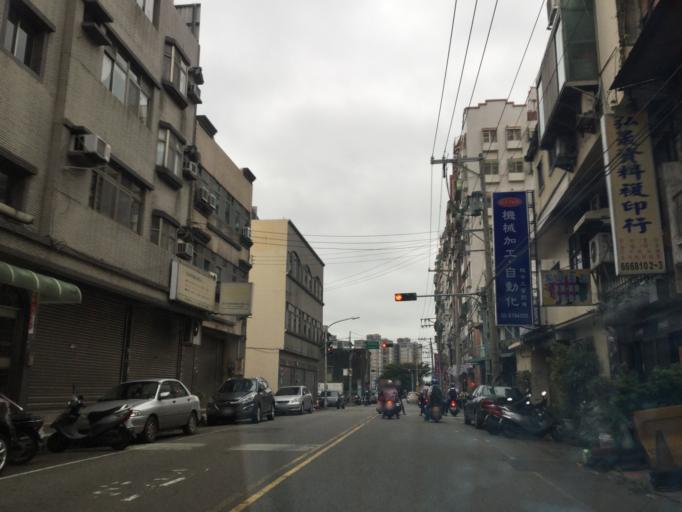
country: TW
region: Taiwan
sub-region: Hsinchu
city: Hsinchu
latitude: 24.7943
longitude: 121.0098
